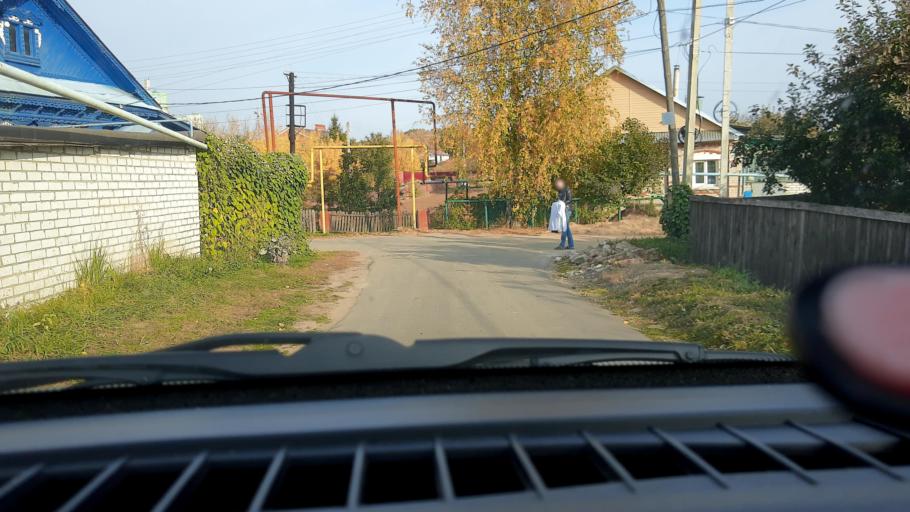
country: RU
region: Nizjnij Novgorod
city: Afonino
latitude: 56.2908
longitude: 44.0955
